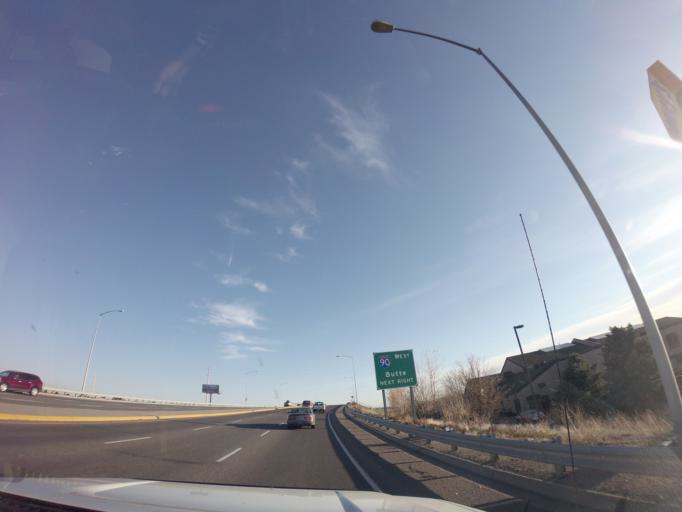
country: US
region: Montana
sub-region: Yellowstone County
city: Billings
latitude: 45.7533
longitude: -108.5629
